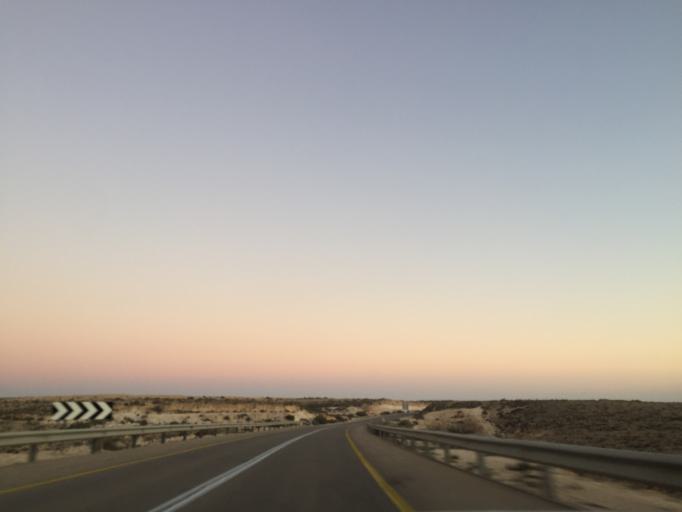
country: IL
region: Southern District
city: Midreshet Ben-Gurion
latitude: 30.8939
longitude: 34.7886
